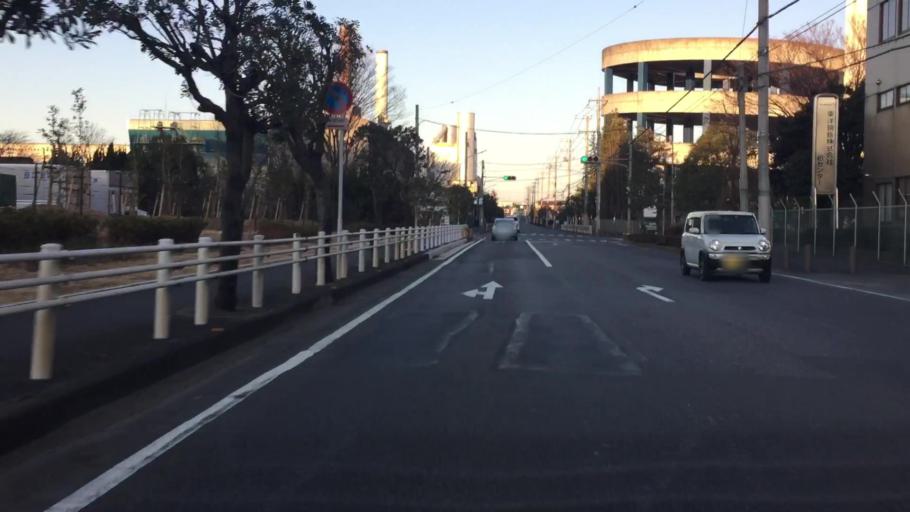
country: JP
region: Chiba
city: Kashiwa
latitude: 35.9082
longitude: 139.9479
